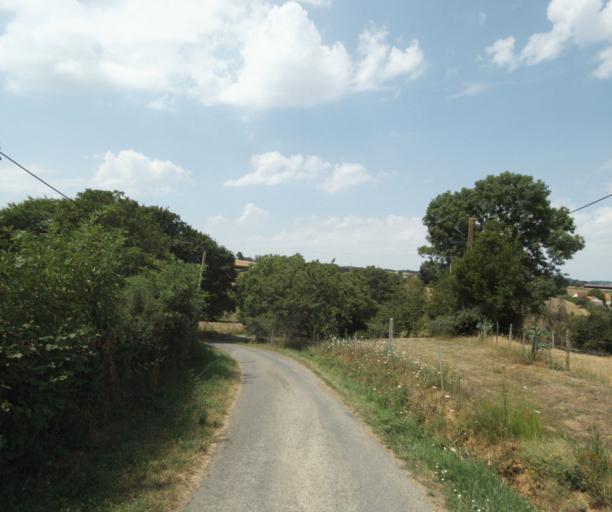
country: FR
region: Bourgogne
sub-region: Departement de Saone-et-Loire
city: Gueugnon
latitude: 46.6130
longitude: 4.0121
